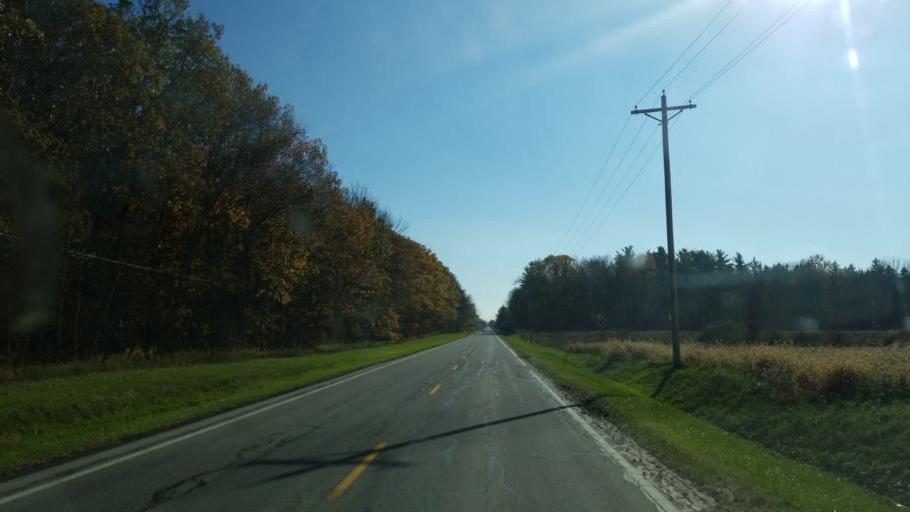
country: US
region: Ohio
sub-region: Lorain County
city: Wellington
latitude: 41.1259
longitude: -82.2193
